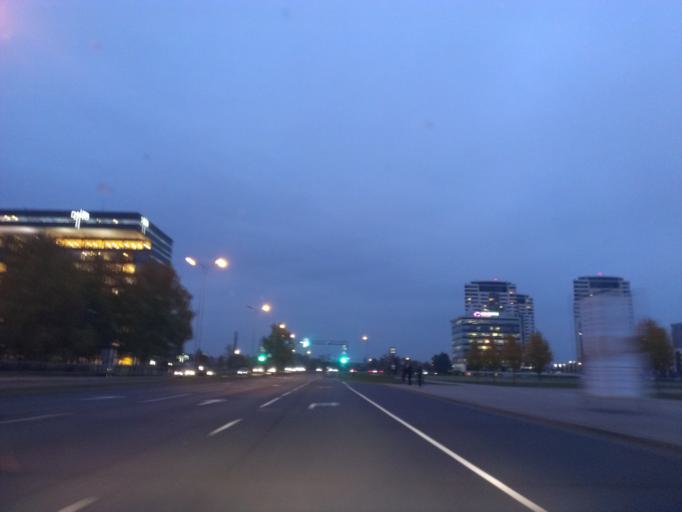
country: LV
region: Riga
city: Riga
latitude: 56.9690
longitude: 24.1190
